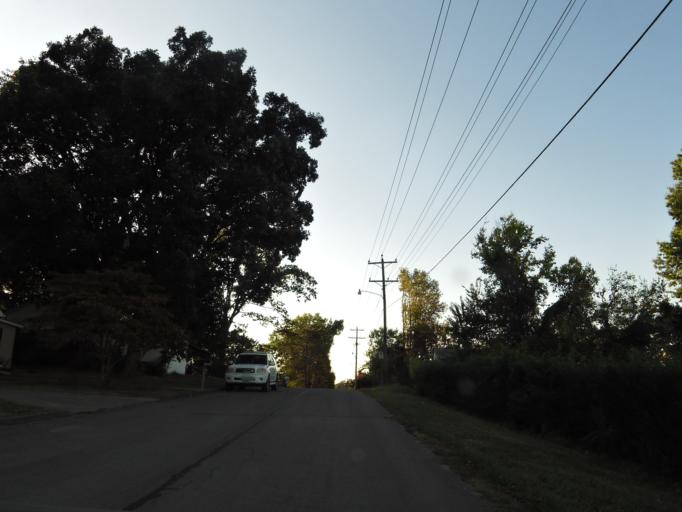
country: US
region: Tennessee
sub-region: Blount County
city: Alcoa
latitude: 35.7994
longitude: -83.9716
